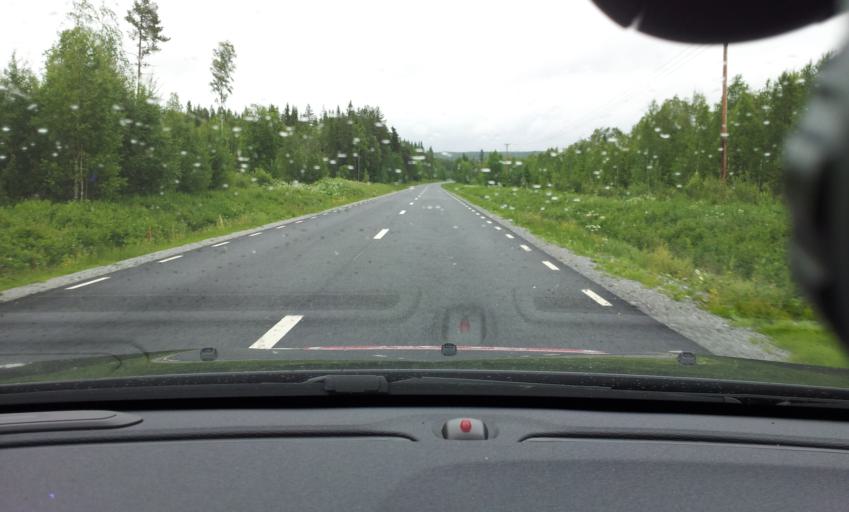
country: SE
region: Jaemtland
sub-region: OEstersunds Kommun
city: Lit
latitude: 63.7392
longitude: 14.7815
